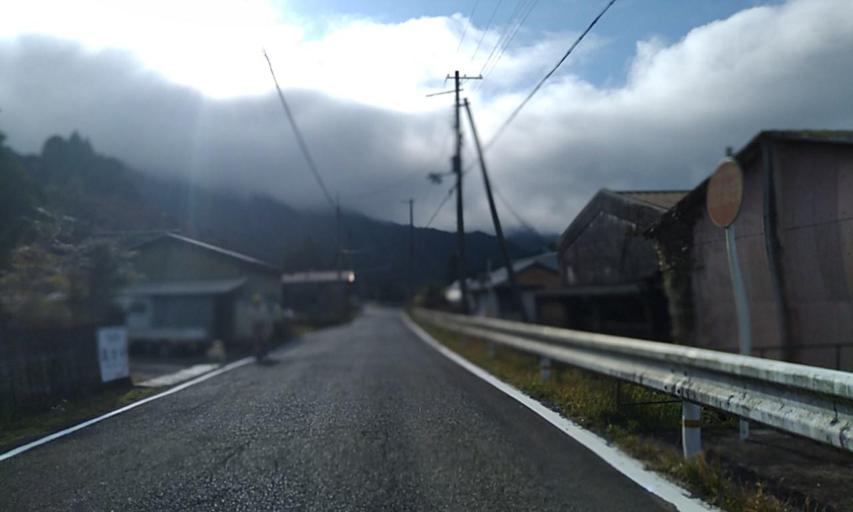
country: JP
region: Wakayama
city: Shingu
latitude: 33.9250
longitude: 135.9834
